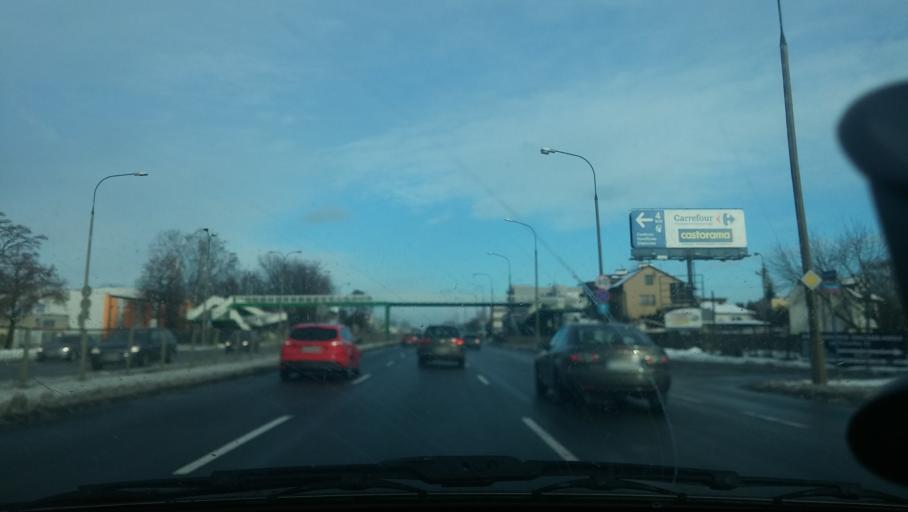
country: PL
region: Masovian Voivodeship
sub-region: Warszawa
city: Targowek
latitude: 52.2828
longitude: 21.0721
